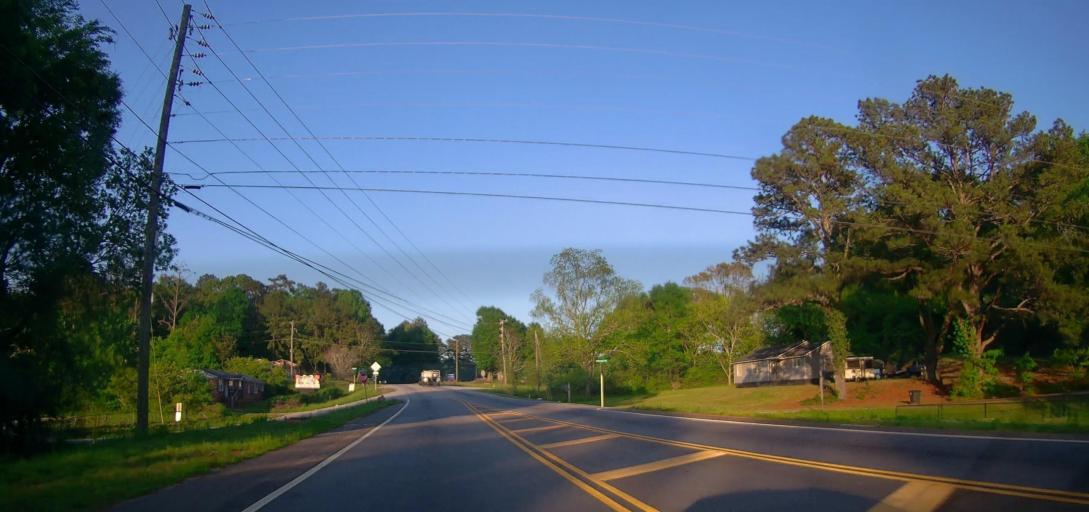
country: US
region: Georgia
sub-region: Newton County
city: Porterdale
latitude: 33.5571
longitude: -83.9201
